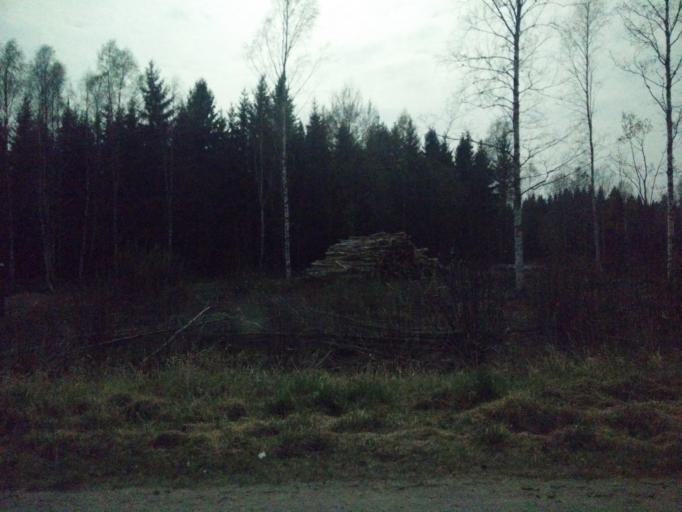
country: SE
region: Vaermland
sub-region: Munkfors Kommun
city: Munkfors
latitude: 59.8363
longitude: 13.5090
